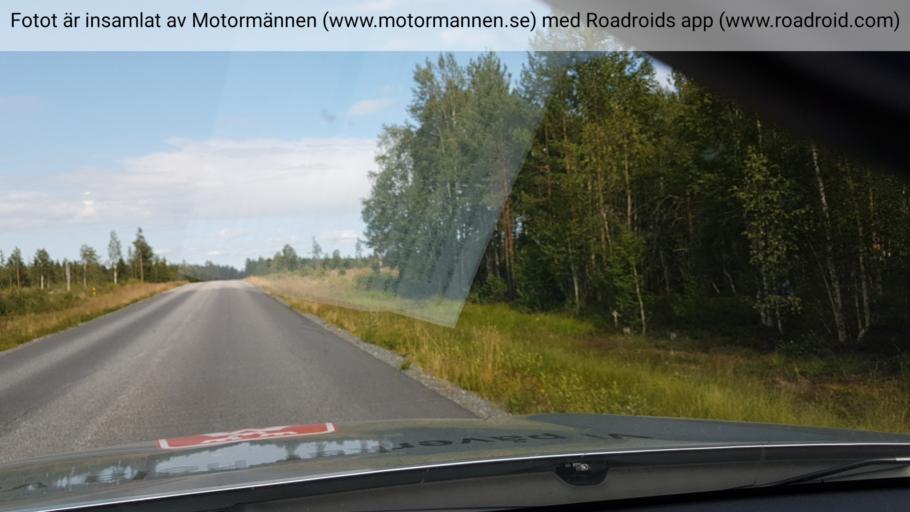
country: SE
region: Vaesterbotten
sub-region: Skelleftea Kommun
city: Boliden
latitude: 65.3047
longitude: 20.2404
